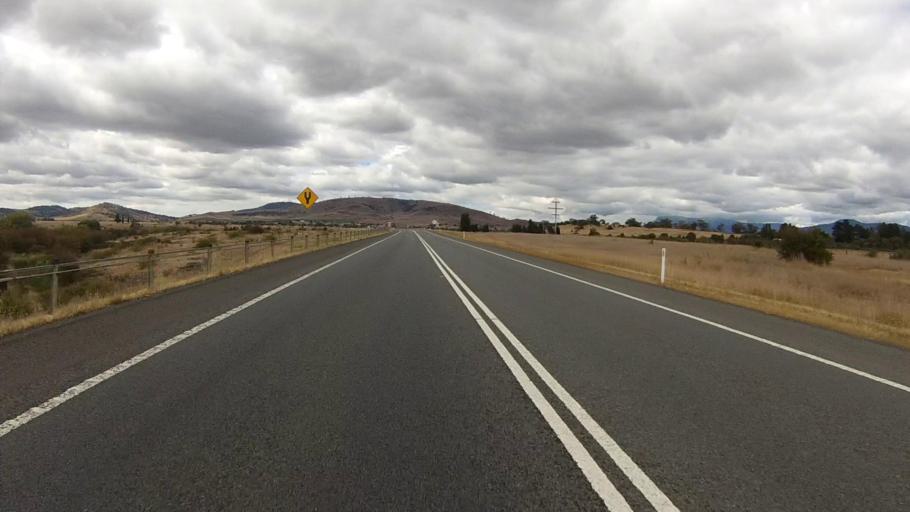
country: AU
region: Tasmania
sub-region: Brighton
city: Bridgewater
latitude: -42.6741
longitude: 147.2694
